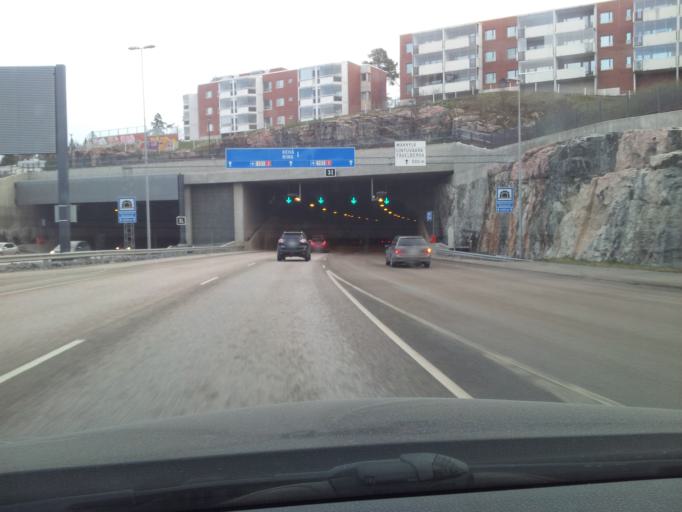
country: FI
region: Uusimaa
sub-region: Helsinki
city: Teekkarikylae
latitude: 60.2205
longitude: 24.8172
